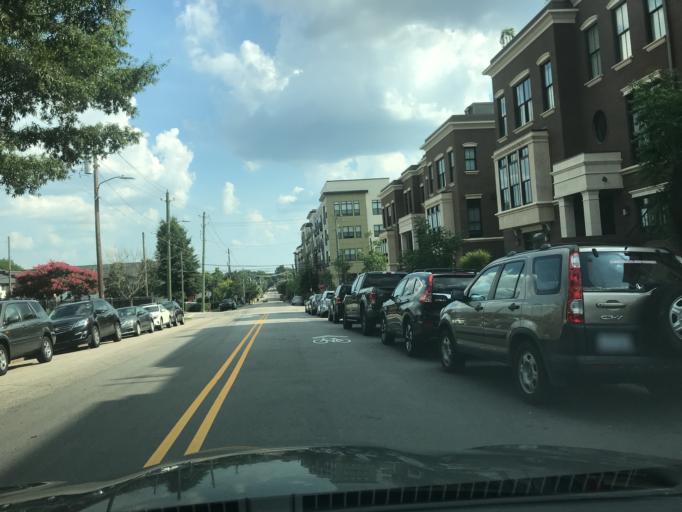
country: US
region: North Carolina
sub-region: Wake County
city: Raleigh
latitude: 35.7787
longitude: -78.6323
